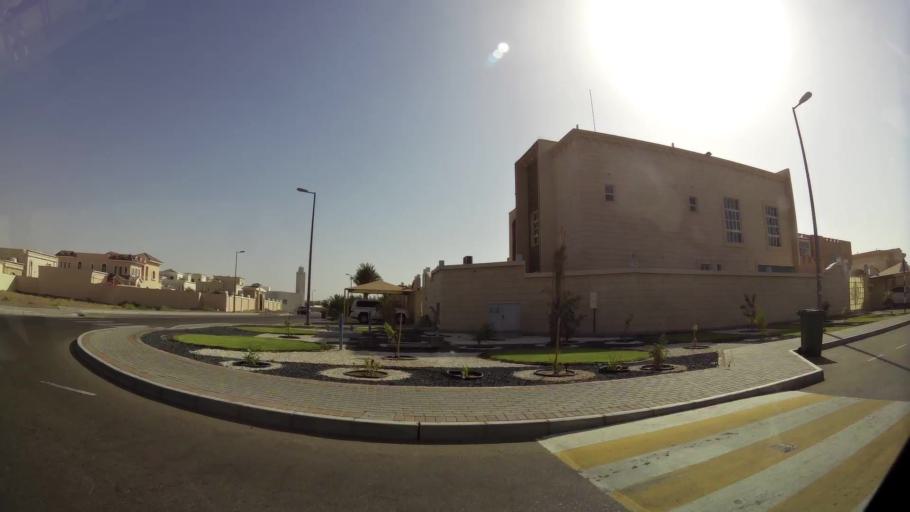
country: OM
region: Al Buraimi
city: Al Buraymi
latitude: 24.3513
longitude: 55.7923
